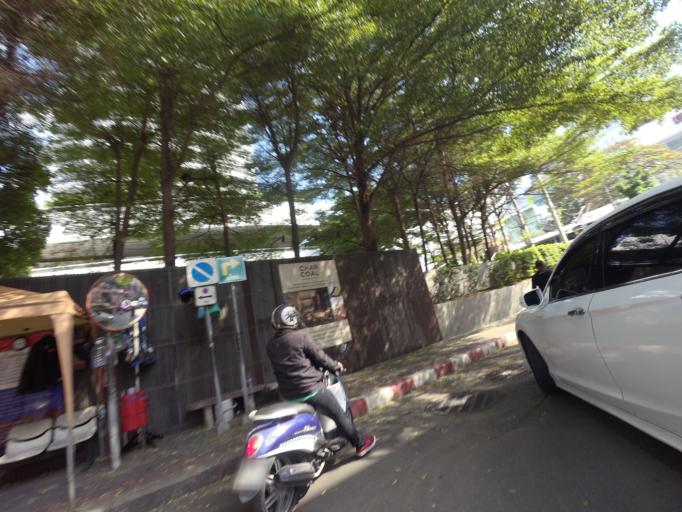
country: TH
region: Bangkok
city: Din Daeng
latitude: 13.7457
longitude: 100.5561
